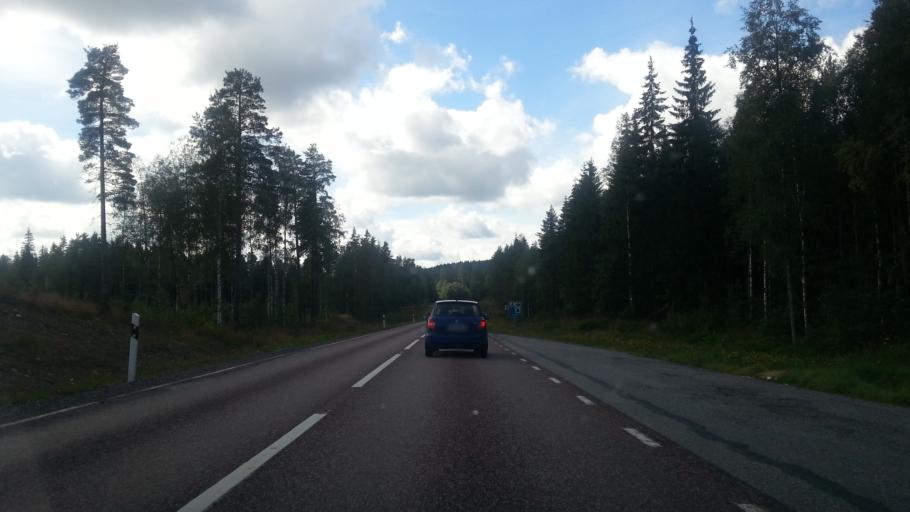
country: SE
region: Dalarna
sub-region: Ludvika Kommun
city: Grangesberg
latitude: 60.0458
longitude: 14.9784
